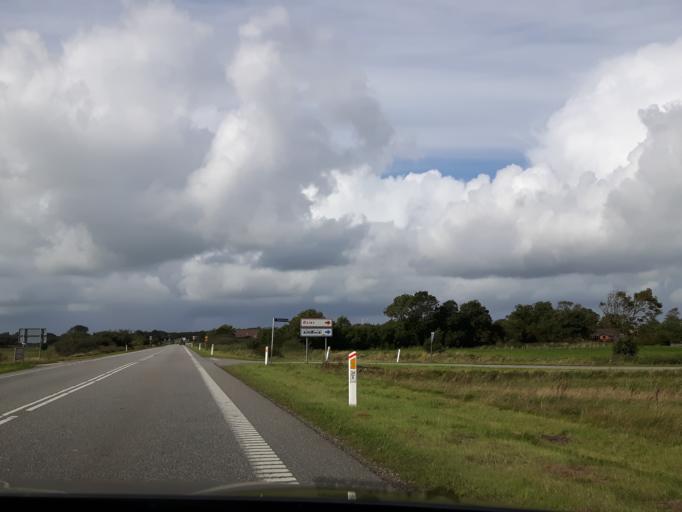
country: DK
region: North Denmark
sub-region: Vesthimmerland Kommune
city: Logstor
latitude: 57.0249
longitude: 9.0134
